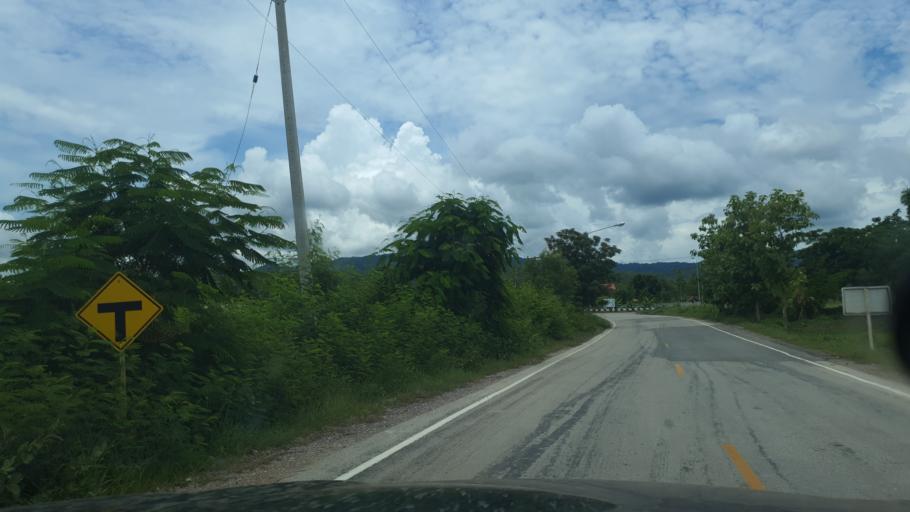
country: TH
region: Lampang
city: Sop Prap
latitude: 17.9213
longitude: 99.4100
